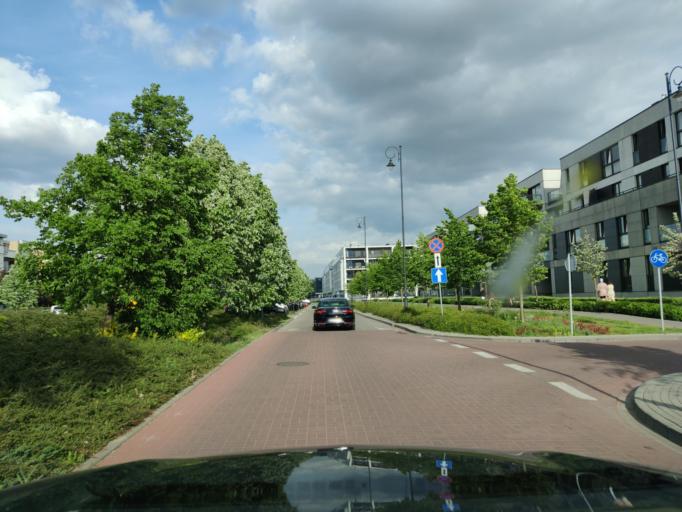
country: PL
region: Masovian Voivodeship
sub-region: Warszawa
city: Wilanow
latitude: 52.1647
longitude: 21.0768
